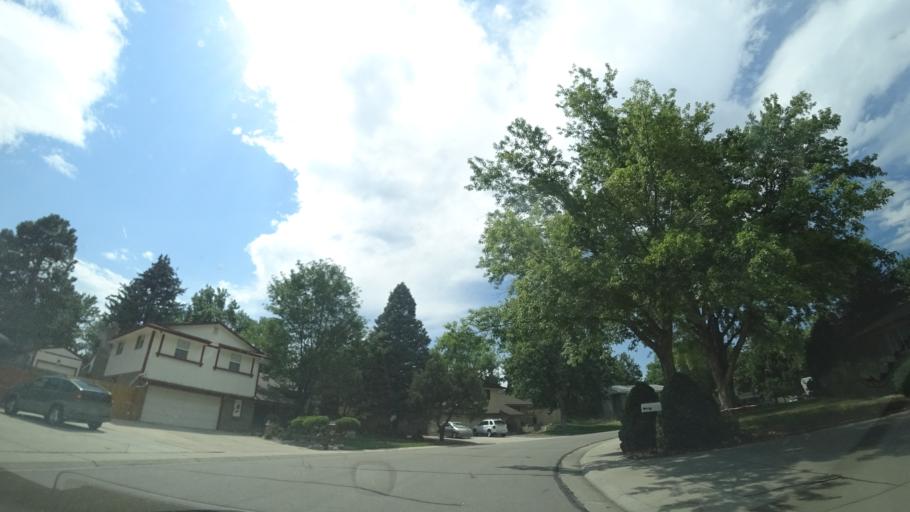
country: US
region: Colorado
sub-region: Jefferson County
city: Lakewood
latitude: 39.6901
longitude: -105.1132
